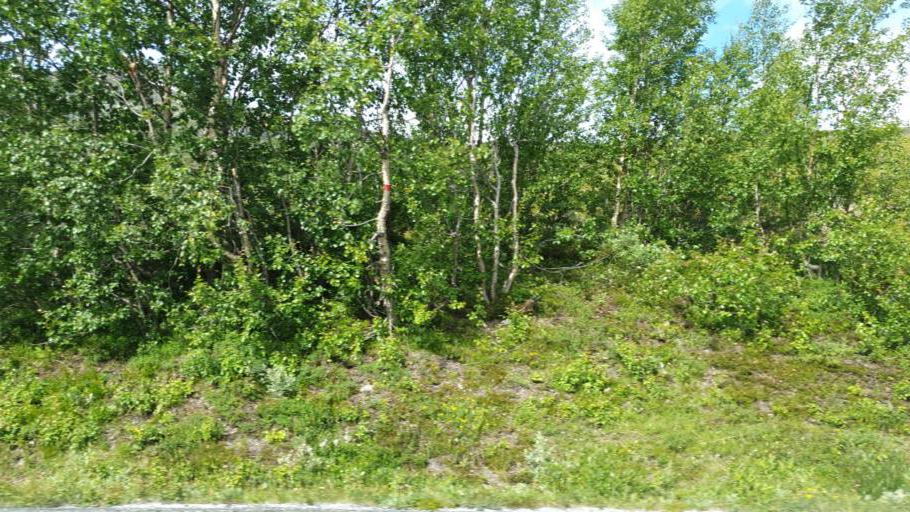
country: NO
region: Oppland
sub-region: Lom
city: Fossbergom
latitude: 61.5113
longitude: 8.8439
